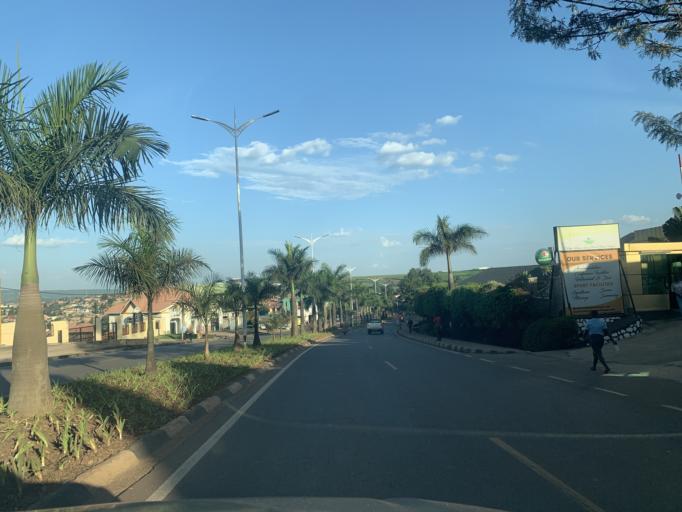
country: RW
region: Kigali
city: Kigali
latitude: -1.9613
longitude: 30.1216
